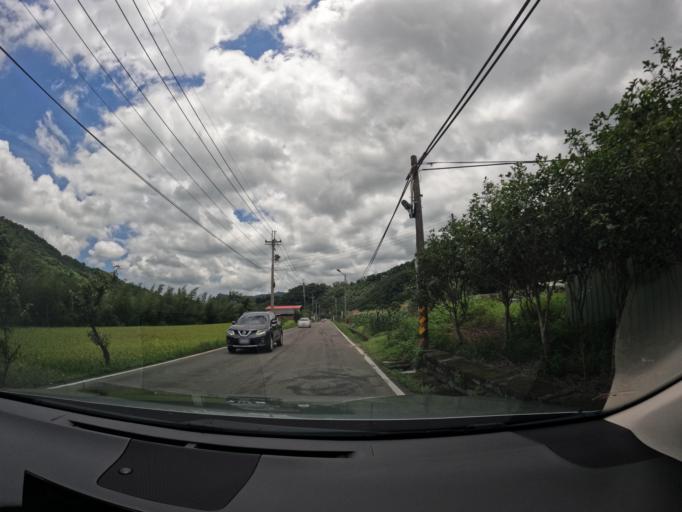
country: TW
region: Taiwan
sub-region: Miaoli
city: Miaoli
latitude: 24.6072
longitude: 121.0025
